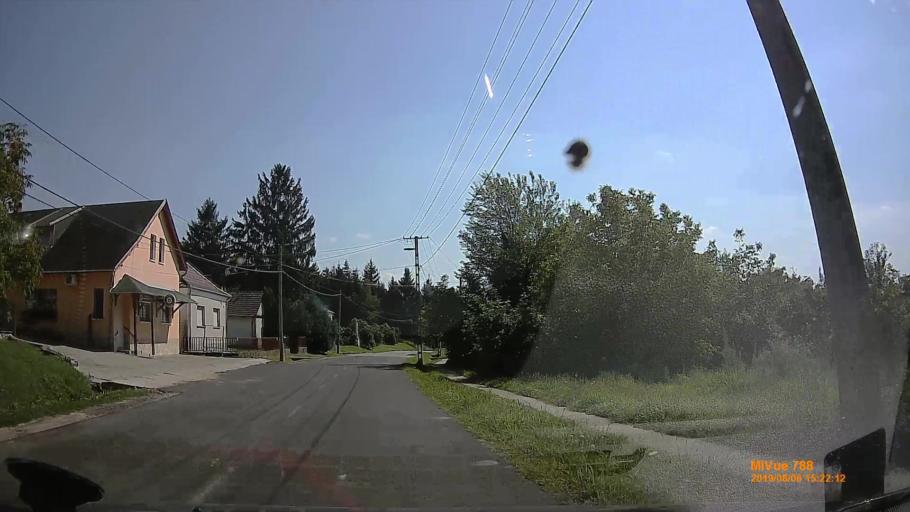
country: HR
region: Koprivnicko-Krizevacka
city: Drnje
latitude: 46.2703
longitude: 16.9478
